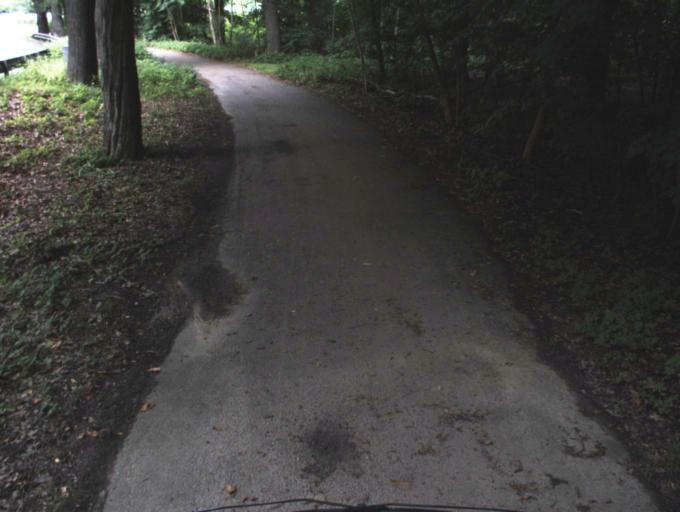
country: SE
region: Skane
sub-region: Helsingborg
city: Helsingborg
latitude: 56.0843
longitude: 12.6641
